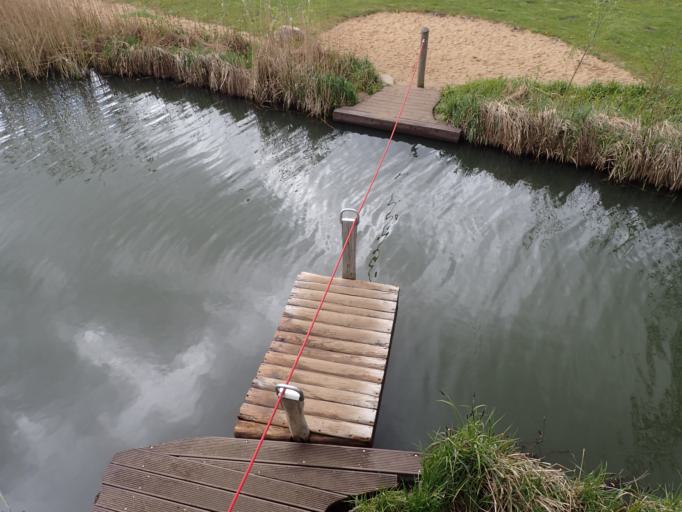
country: DE
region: Brandenburg
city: Luebben
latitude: 51.9356
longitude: 13.8961
